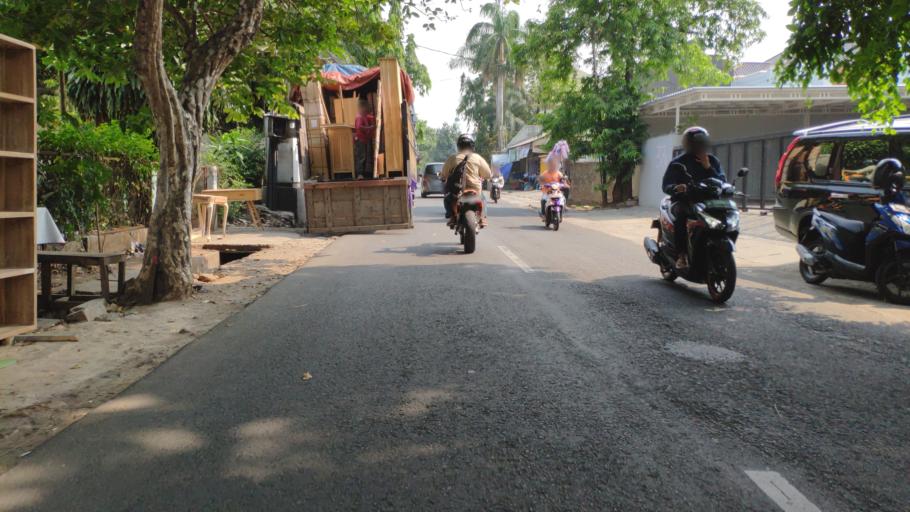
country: ID
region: Jakarta Raya
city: Jakarta
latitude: -6.2644
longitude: 106.8238
